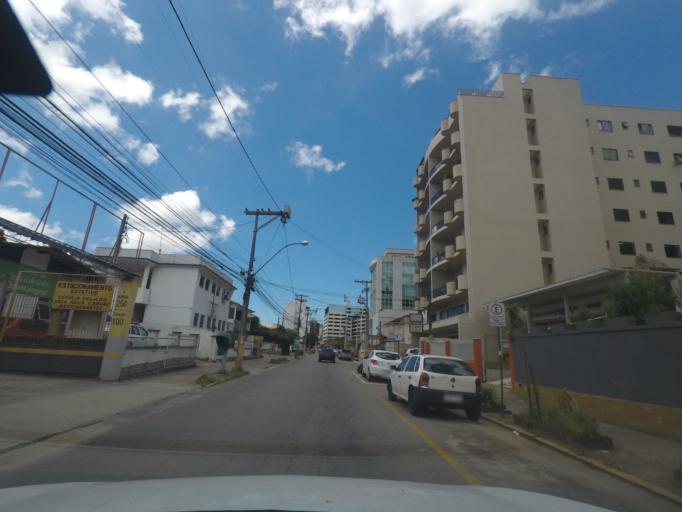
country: BR
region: Rio de Janeiro
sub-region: Teresopolis
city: Teresopolis
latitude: -22.4075
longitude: -42.9674
